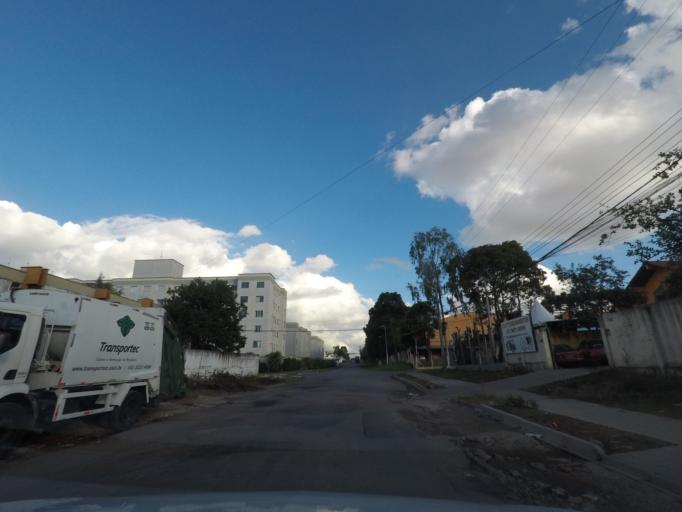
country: BR
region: Parana
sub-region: Curitiba
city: Curitiba
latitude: -25.4824
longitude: -49.2622
